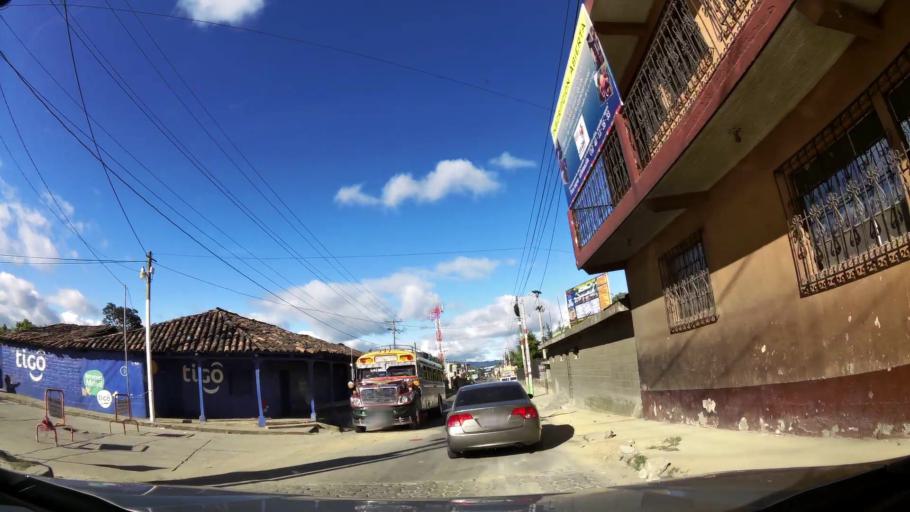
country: GT
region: Quiche
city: Chichicastenango
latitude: 14.9499
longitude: -91.1086
